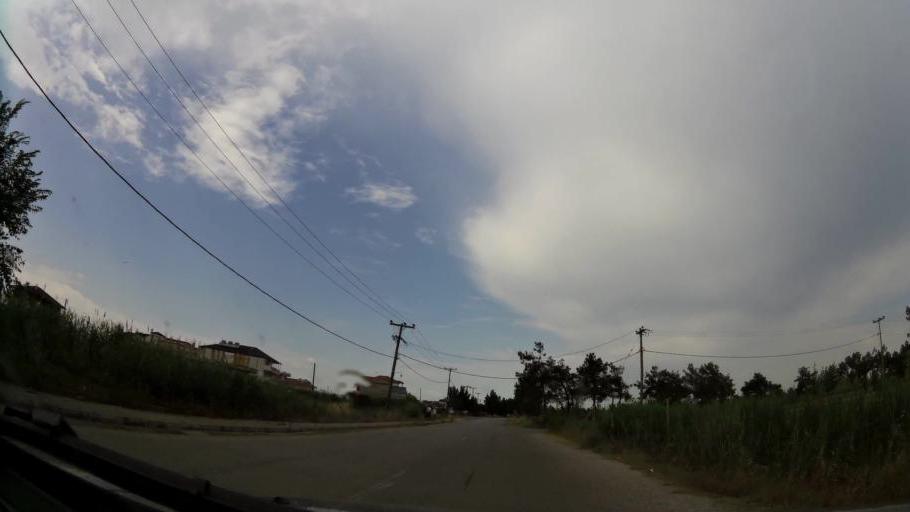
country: GR
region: Central Macedonia
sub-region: Nomos Pierias
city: Paralia
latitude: 40.2733
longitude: 22.5956
